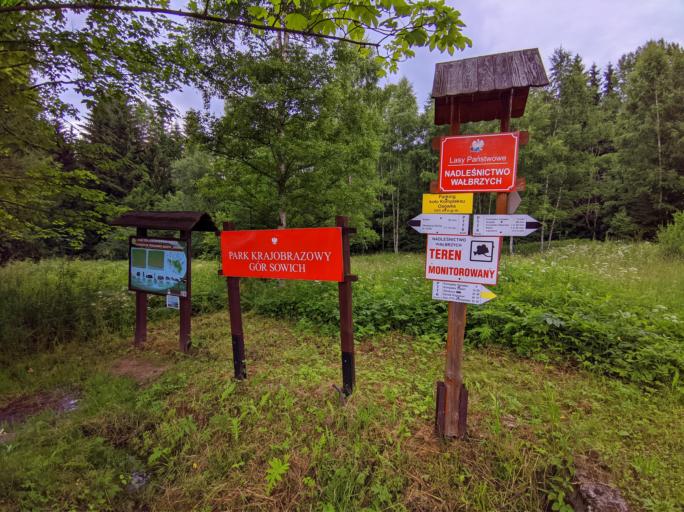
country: PL
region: Lower Silesian Voivodeship
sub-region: Powiat walbrzyski
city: Walim
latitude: 50.6698
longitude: 16.4179
